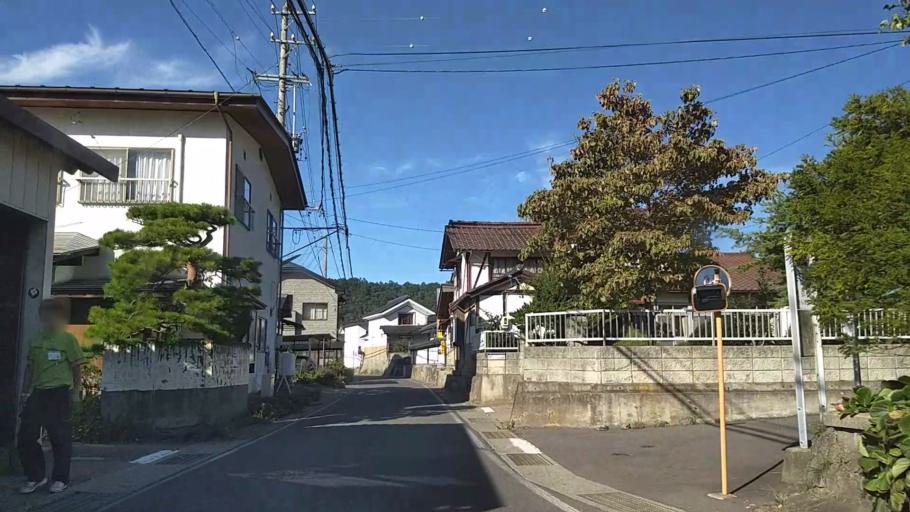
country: JP
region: Nagano
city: Nagano-shi
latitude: 36.5499
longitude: 138.1558
